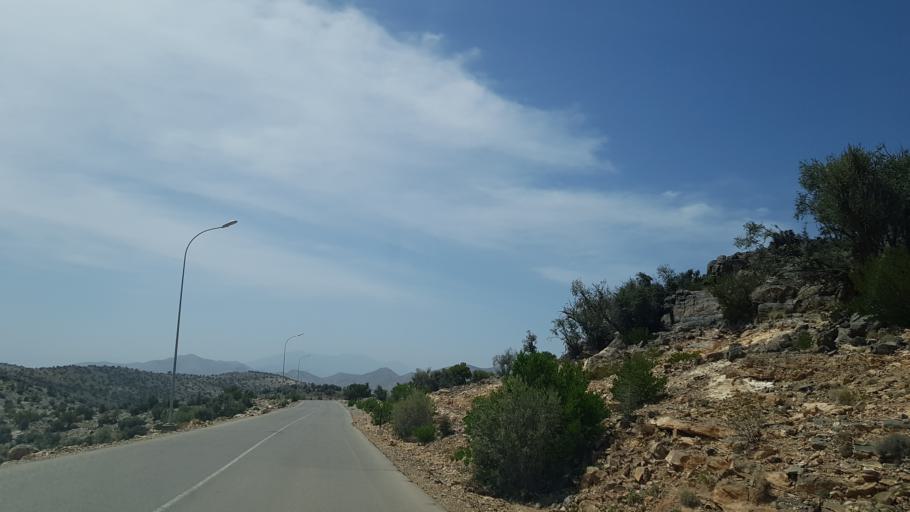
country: OM
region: Al Batinah
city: Bayt al `Awabi
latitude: 23.1401
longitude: 57.5915
